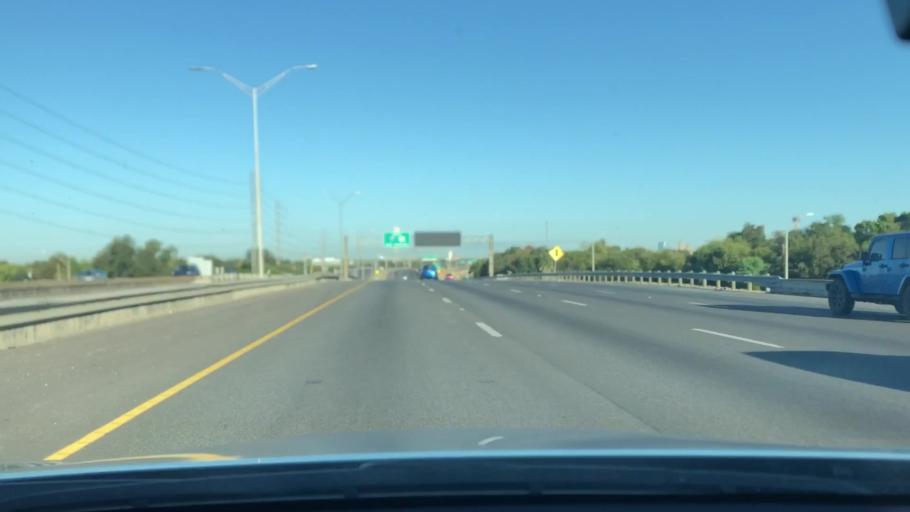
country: US
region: Texas
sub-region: Bexar County
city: San Antonio
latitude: 29.3842
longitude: -98.4693
